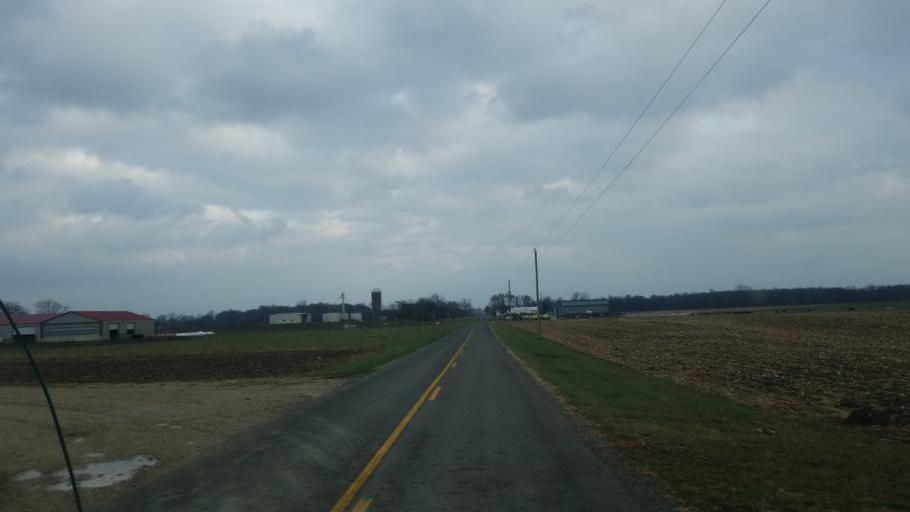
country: US
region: Ohio
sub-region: Mercer County
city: Fort Recovery
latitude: 40.5090
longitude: -84.7541
